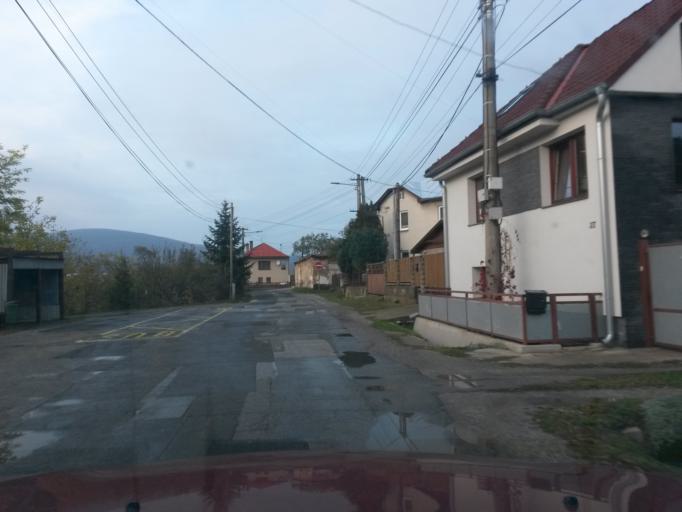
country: SK
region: Kosicky
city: Kosice
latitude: 48.7759
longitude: 21.2058
